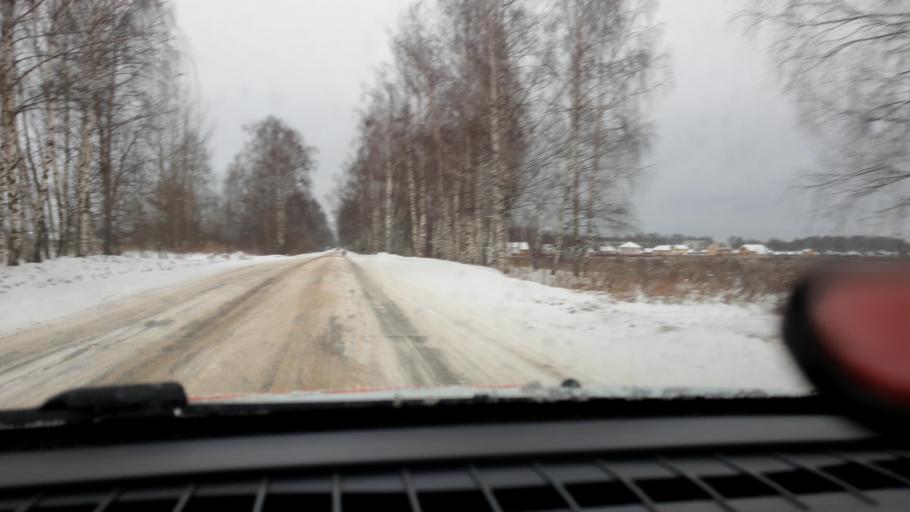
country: RU
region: Nizjnij Novgorod
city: Pamyat' Parizhskoy Kommuny
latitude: 56.2667
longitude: 44.4324
